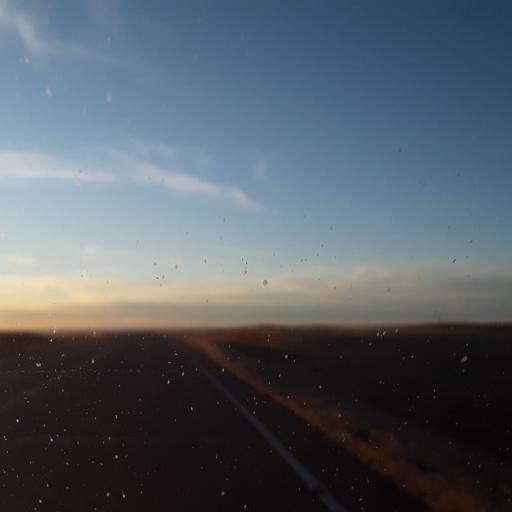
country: US
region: Colorado
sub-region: Cheyenne County
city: Cheyenne Wells
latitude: 38.8159
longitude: -102.5508
